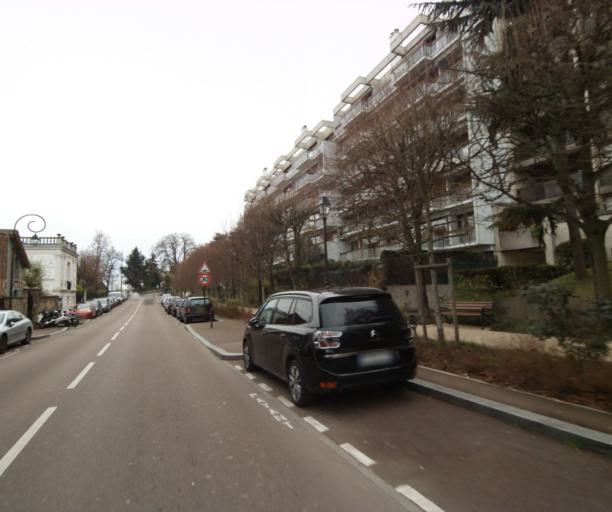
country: FR
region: Ile-de-France
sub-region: Departement des Hauts-de-Seine
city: Saint-Cloud
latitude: 48.8516
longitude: 2.2166
